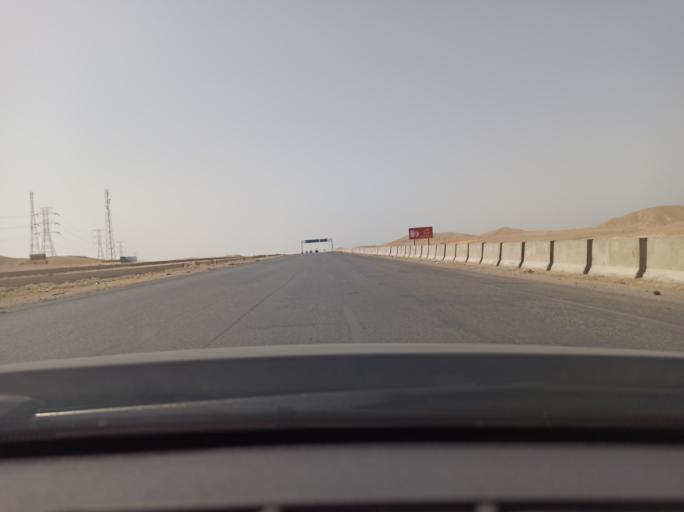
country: EG
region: Al Jizah
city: As Saff
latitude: 29.5419
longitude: 31.3908
